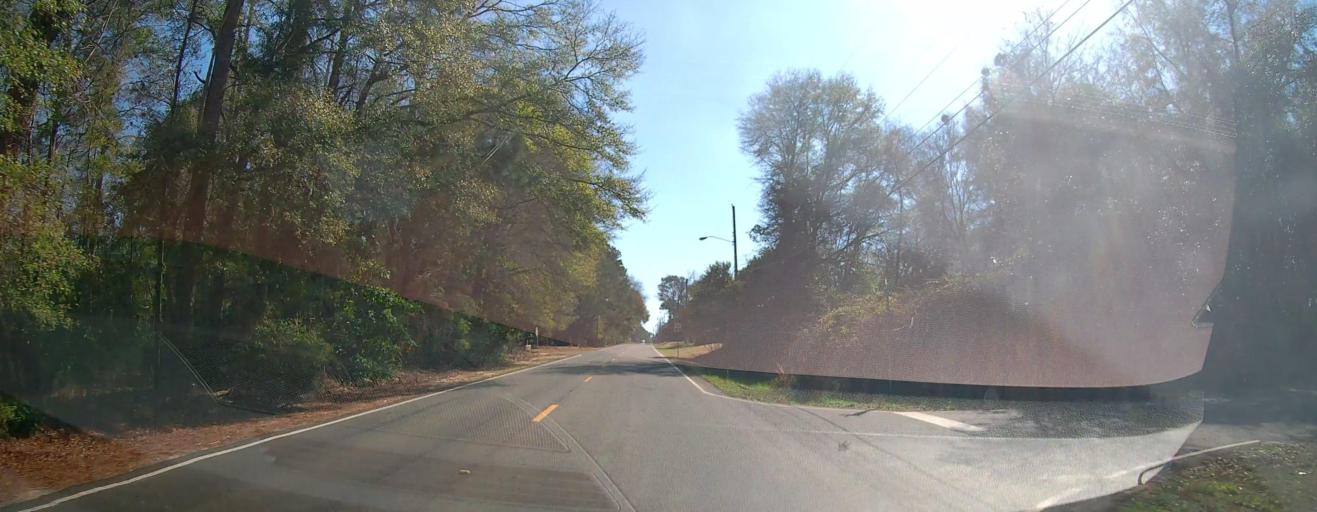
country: US
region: Georgia
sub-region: Macon County
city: Montezuma
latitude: 32.3207
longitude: -84.0230
